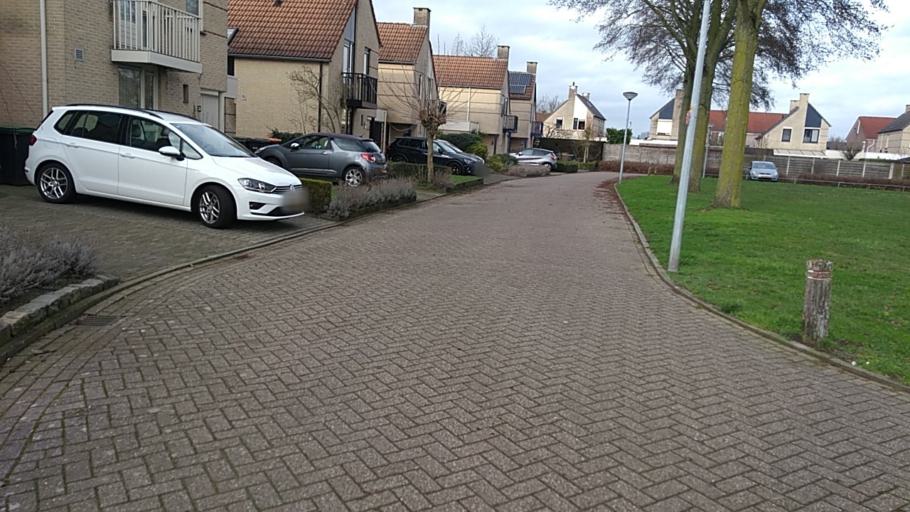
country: NL
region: Overijssel
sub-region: Gemeente Almelo
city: Almelo
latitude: 52.3738
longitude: 6.6811
